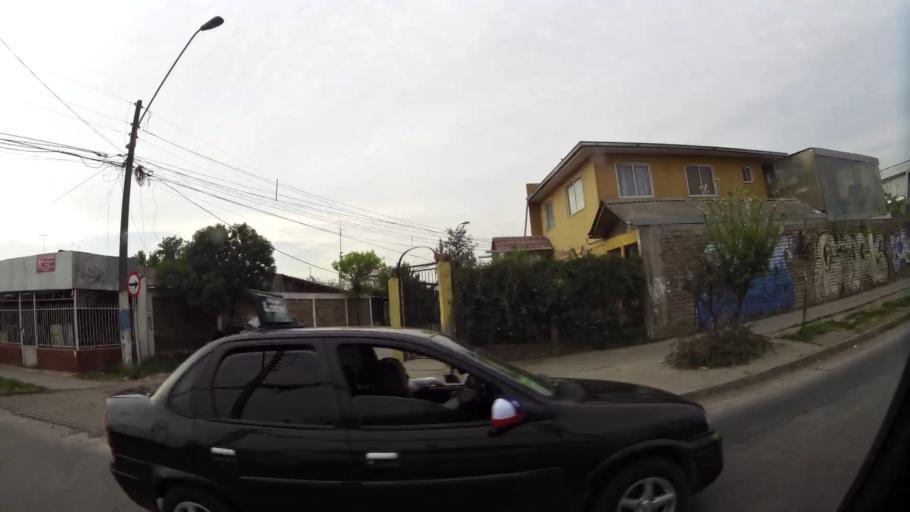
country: CL
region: Santiago Metropolitan
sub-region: Provincia de Santiago
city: Lo Prado
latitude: -33.5120
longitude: -70.7772
